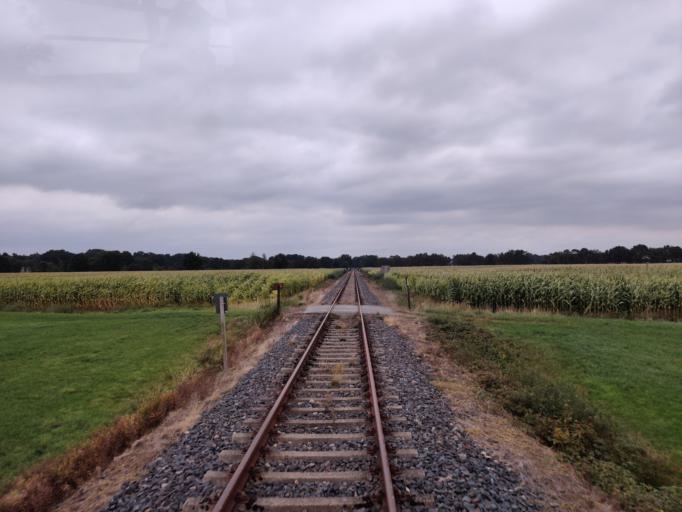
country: DE
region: Lower Saxony
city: Vollersode
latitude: 53.2853
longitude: 8.9681
